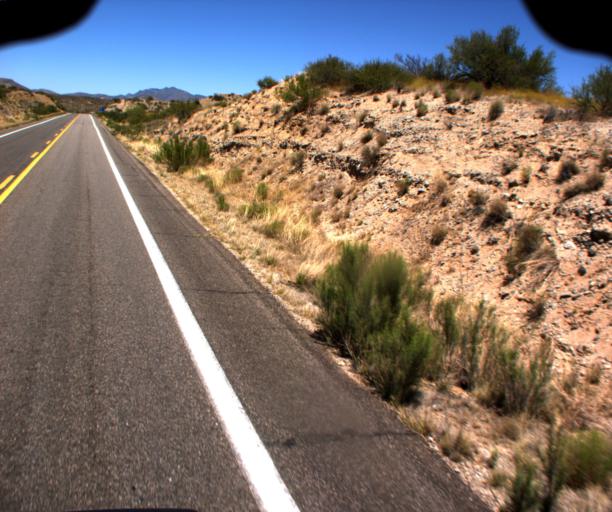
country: US
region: Arizona
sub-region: Gila County
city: Globe
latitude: 33.3610
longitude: -110.7360
